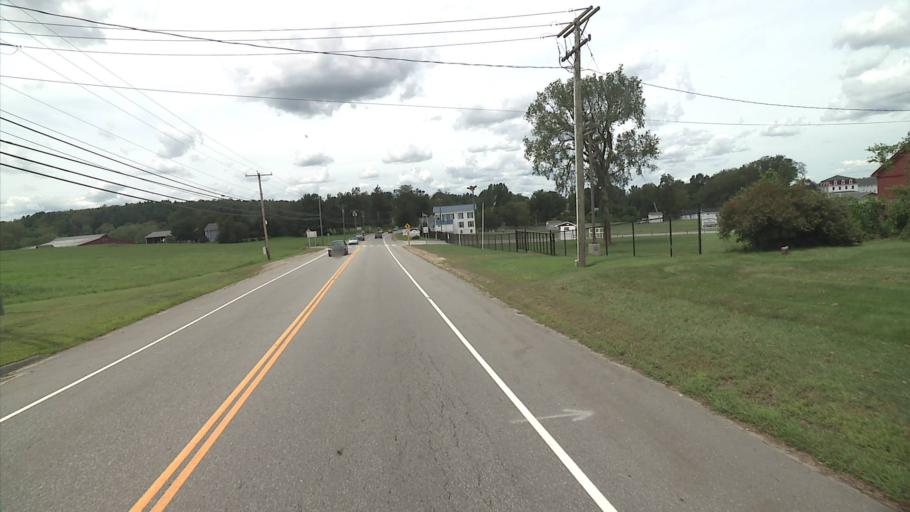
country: US
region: Connecticut
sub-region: Windham County
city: South Woodstock
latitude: 41.9346
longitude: -71.9571
